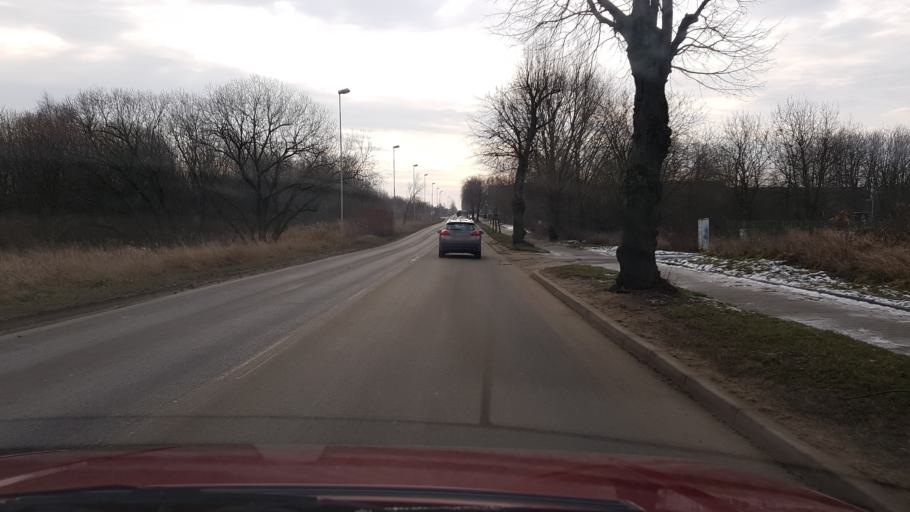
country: PL
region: West Pomeranian Voivodeship
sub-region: Powiat policki
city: Police
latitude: 53.4905
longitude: 14.5847
